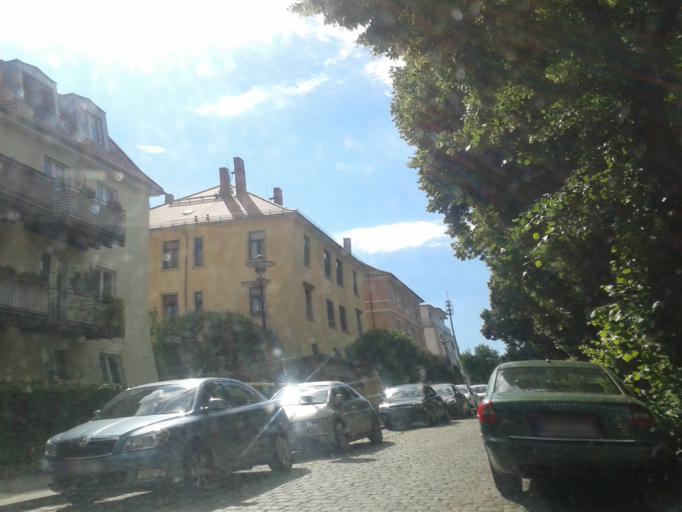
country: DE
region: Saxony
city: Freital
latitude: 51.0513
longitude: 13.6767
